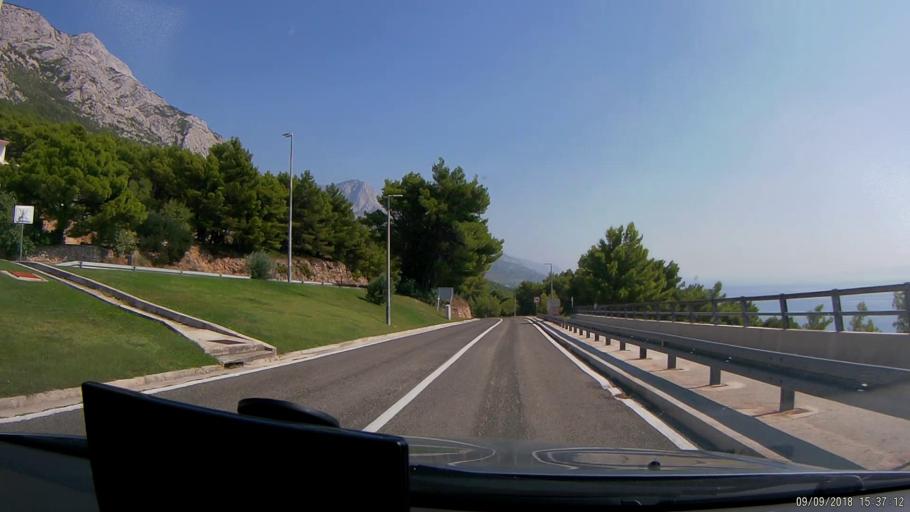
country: HR
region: Splitsko-Dalmatinska
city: Donja Brela
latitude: 43.3743
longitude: 16.9263
